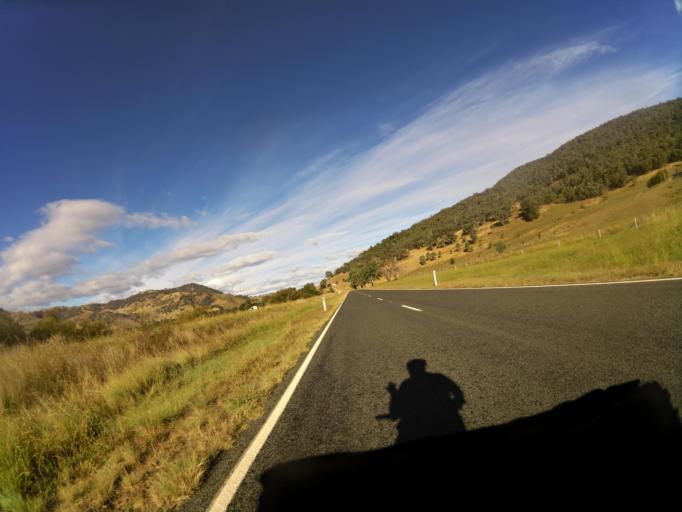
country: AU
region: New South Wales
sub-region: Greater Hume Shire
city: Holbrook
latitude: -35.9720
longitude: 147.7958
